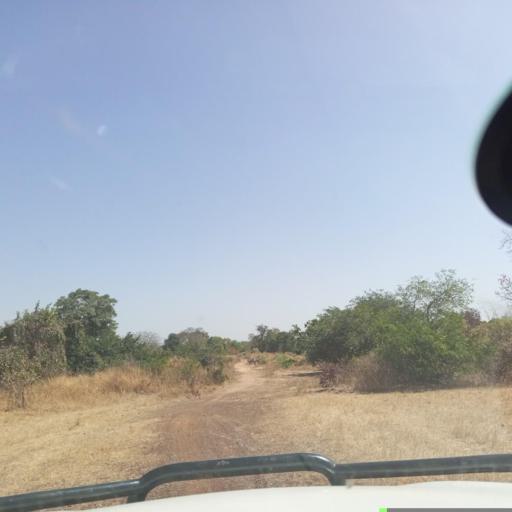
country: ML
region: Koulikoro
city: Dioila
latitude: 12.5671
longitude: -6.9557
